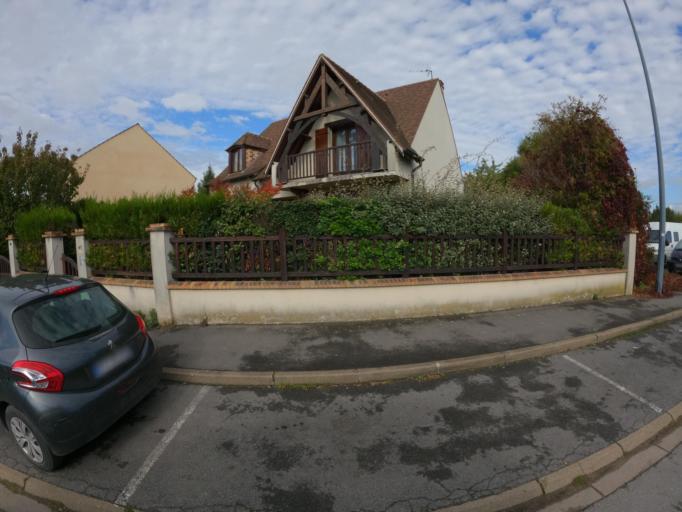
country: FR
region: Ile-de-France
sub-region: Departement de Seine-et-Marne
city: Brou-sur-Chantereine
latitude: 48.8852
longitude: 2.6215
